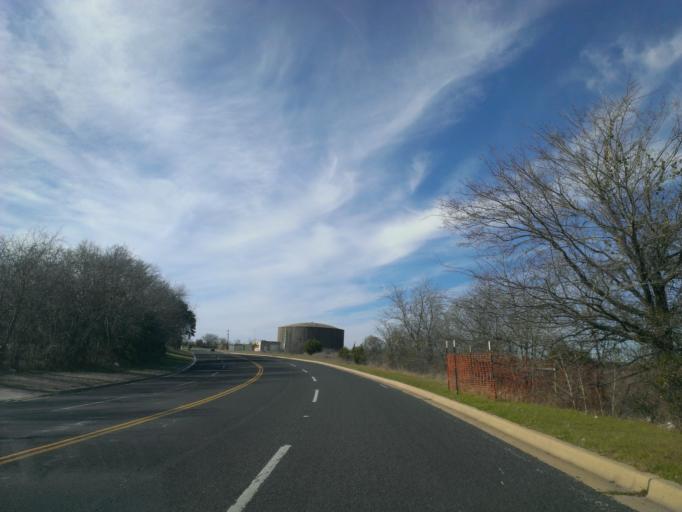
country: US
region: Texas
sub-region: Bell County
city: Killeen
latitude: 31.1387
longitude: -97.7000
